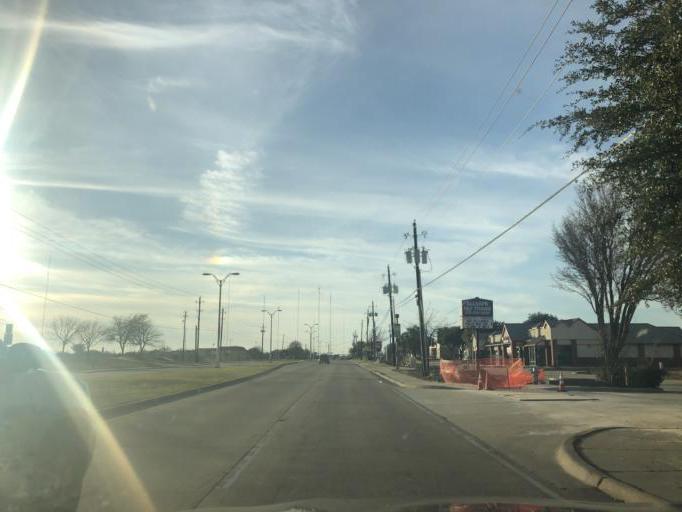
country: US
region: Texas
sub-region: Dallas County
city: Cedar Hill
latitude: 32.5900
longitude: -96.9281
